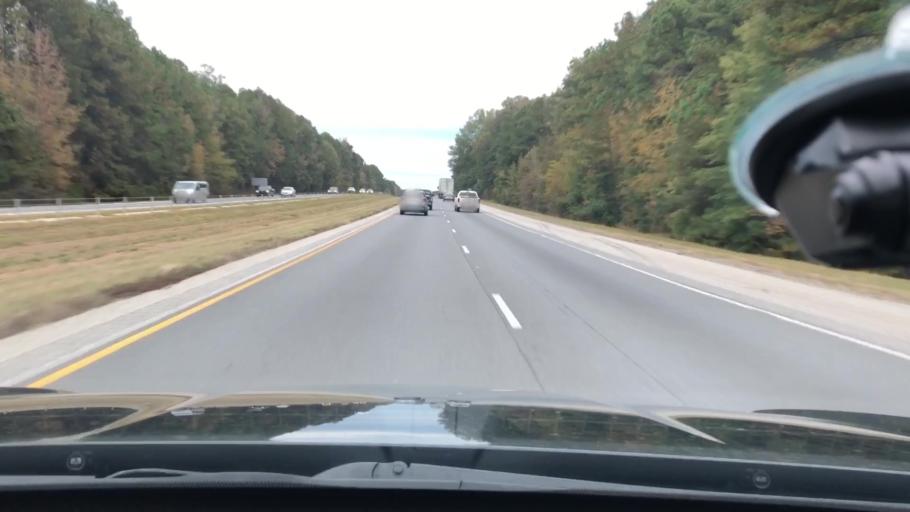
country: US
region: Arkansas
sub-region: Clark County
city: Arkadelphia
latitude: 34.1254
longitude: -93.0892
